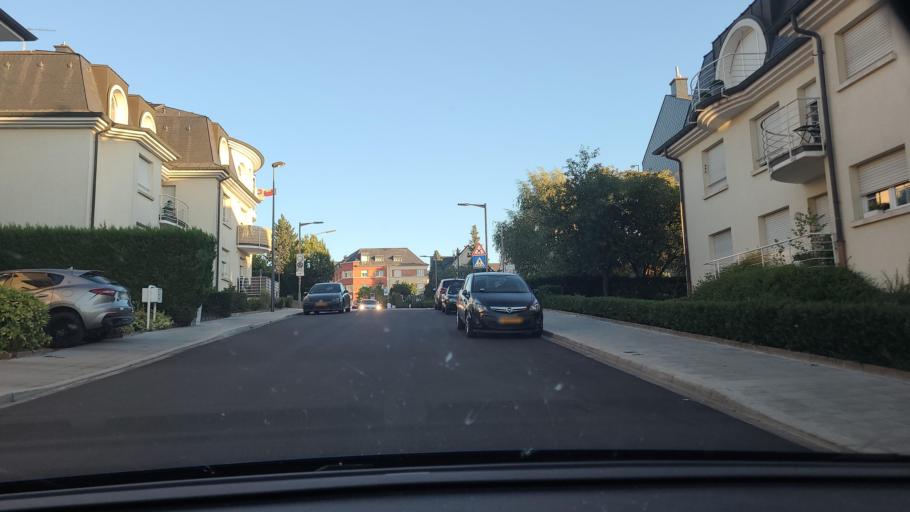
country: LU
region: Luxembourg
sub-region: Canton de Luxembourg
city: Luxembourg
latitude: 49.5993
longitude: 6.1494
